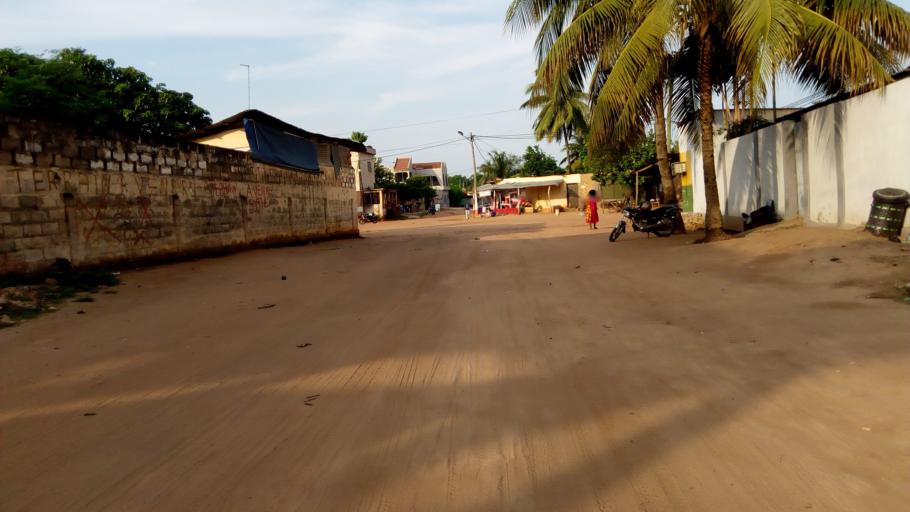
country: TG
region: Maritime
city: Lome
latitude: 6.1856
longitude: 1.1840
